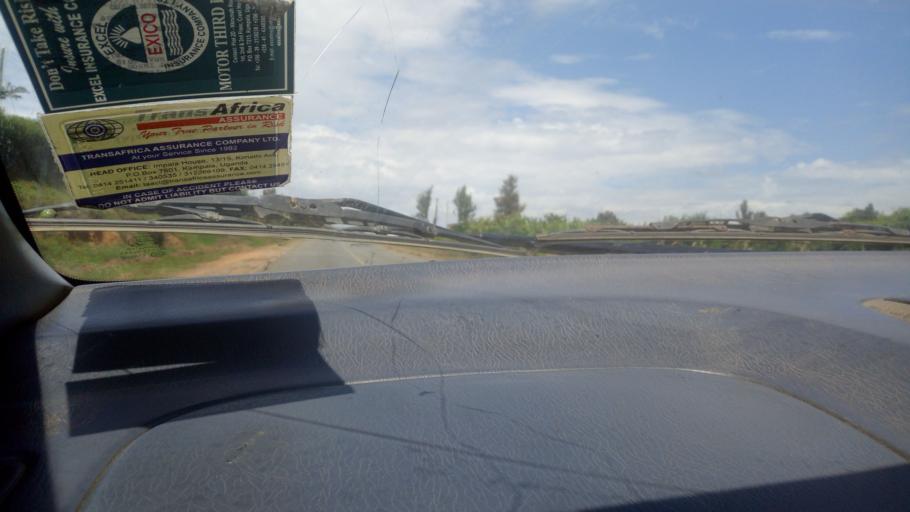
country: UG
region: Western Region
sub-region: Buhweju District
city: Buhweju
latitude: -0.2671
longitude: 30.5612
